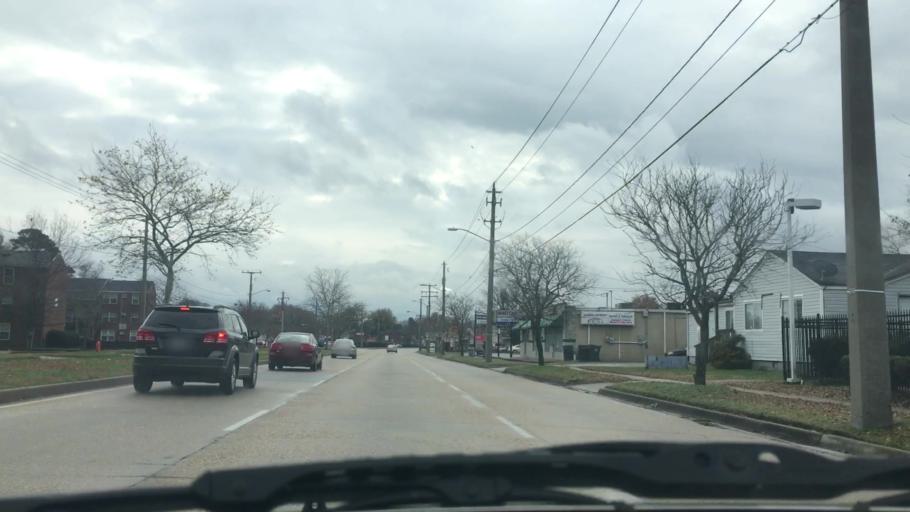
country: US
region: Virginia
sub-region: City of Norfolk
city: Norfolk
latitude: 36.8934
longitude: -76.2382
